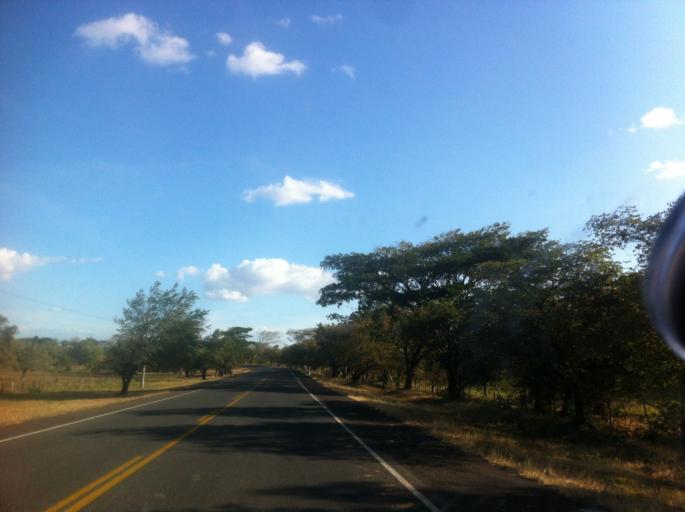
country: NI
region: Chontales
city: Acoyapa
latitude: 11.9323
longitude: -85.1430
